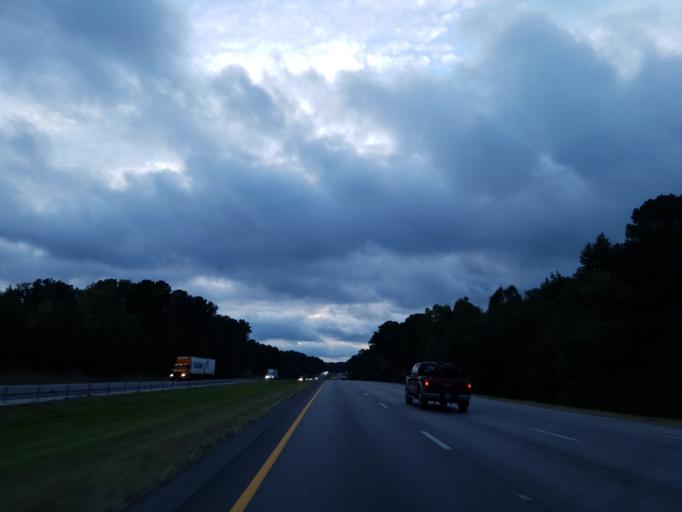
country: US
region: Mississippi
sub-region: Lauderdale County
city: Marion
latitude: 32.3949
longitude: -88.5830
